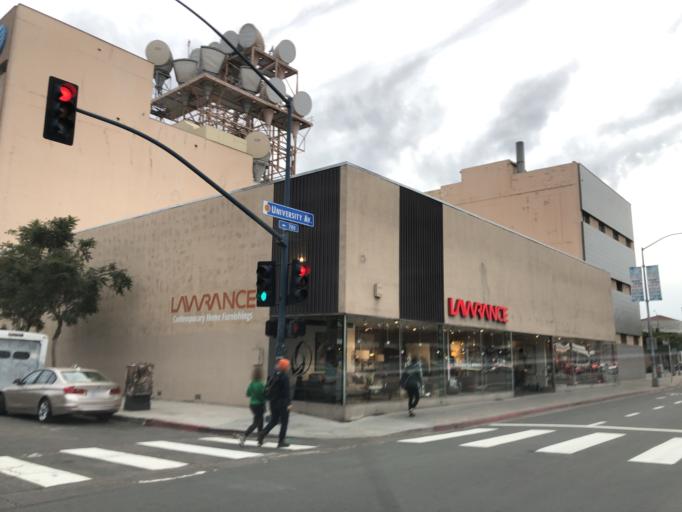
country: US
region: California
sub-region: San Diego County
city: San Diego
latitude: 32.7484
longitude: -117.1584
